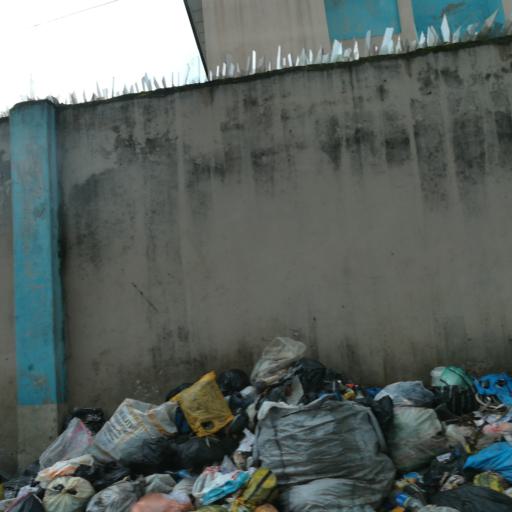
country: NG
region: Lagos
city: Agege
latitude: 6.5964
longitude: 3.2962
